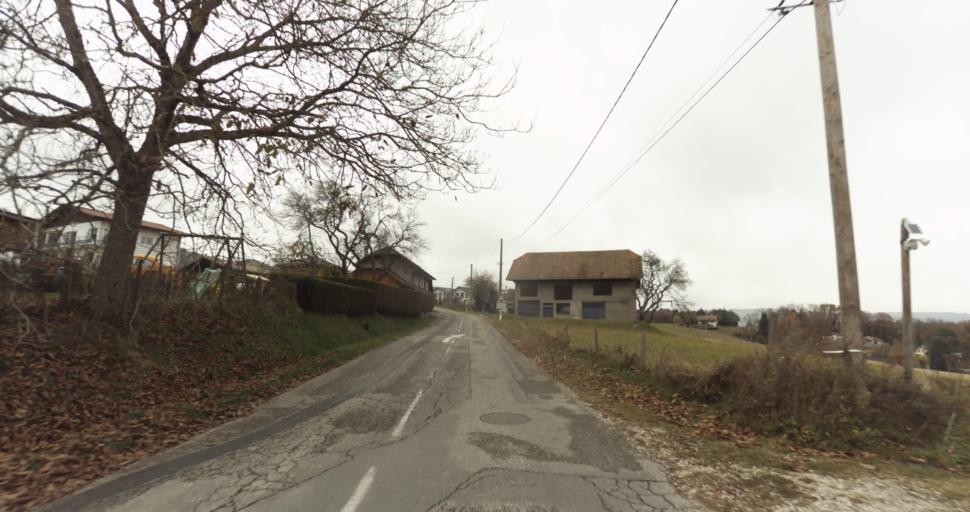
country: FR
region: Rhone-Alpes
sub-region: Departement de la Haute-Savoie
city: Saint-Martin-Bellevue
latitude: 45.9812
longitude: 6.1585
